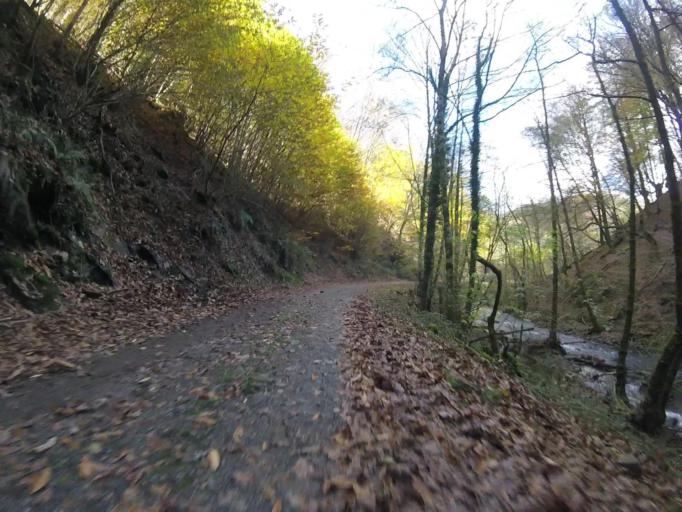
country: ES
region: Navarre
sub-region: Provincia de Navarra
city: Goizueta
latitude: 43.2136
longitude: -1.8003
